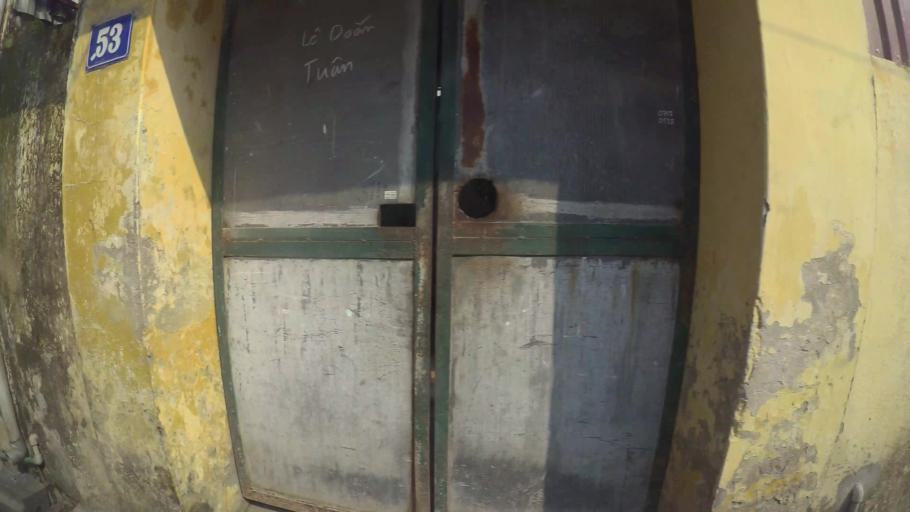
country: VN
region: Ha Noi
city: Ha Dong
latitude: 20.9934
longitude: 105.7550
